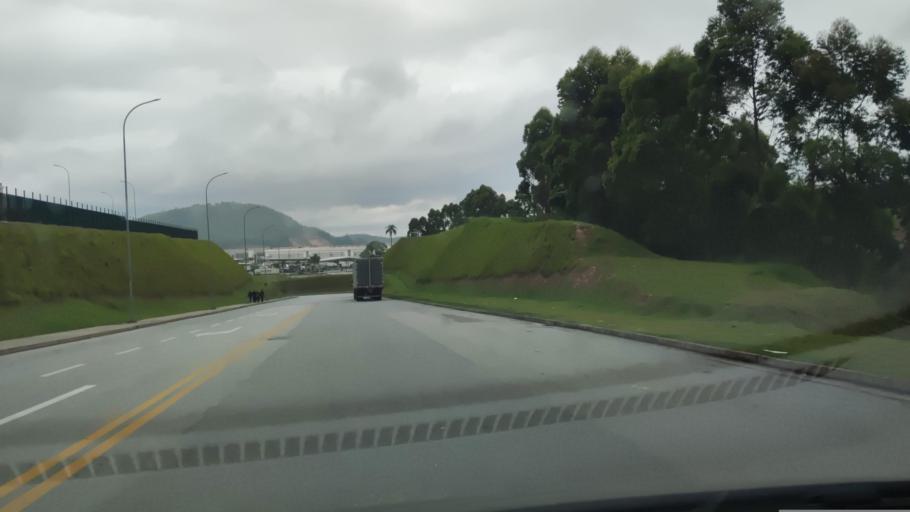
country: BR
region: Sao Paulo
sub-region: Cajamar
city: Cajamar
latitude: -23.3304
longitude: -46.8516
